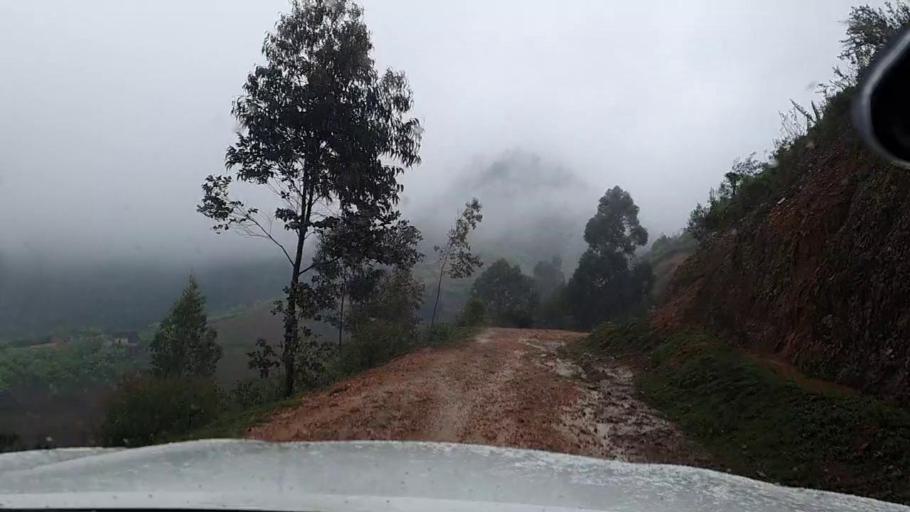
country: RW
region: Western Province
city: Kibuye
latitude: -2.1348
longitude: 29.4609
